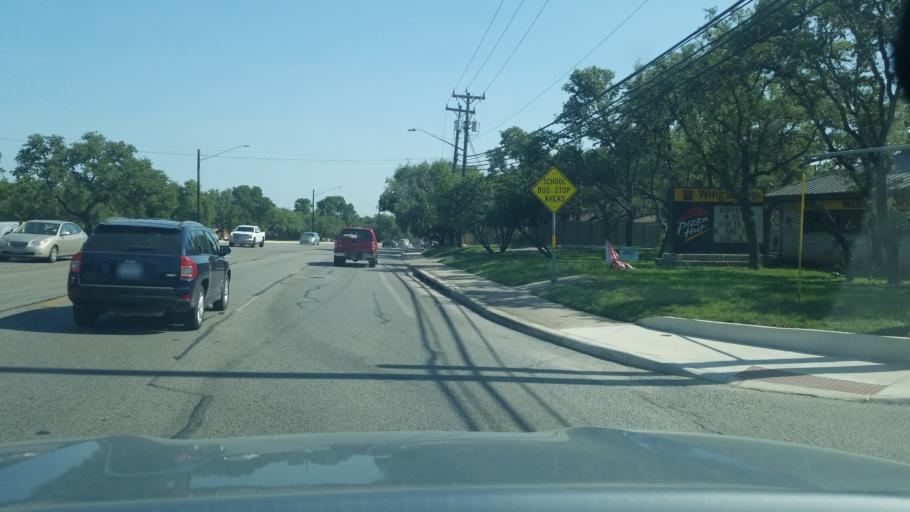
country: US
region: Texas
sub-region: Bexar County
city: Hollywood Park
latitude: 29.6021
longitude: -98.5081
